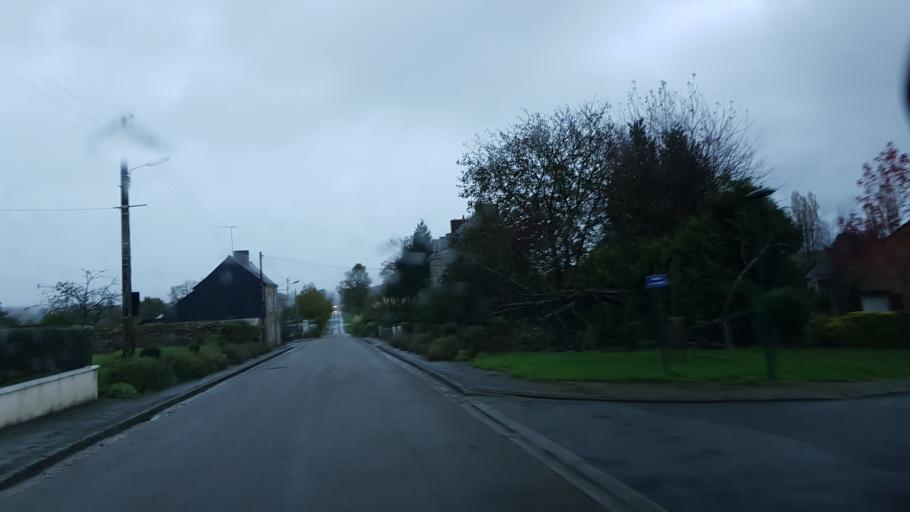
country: FR
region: Pays de la Loire
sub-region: Departement de la Mayenne
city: Juvigne
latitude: 48.2311
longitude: -1.0327
